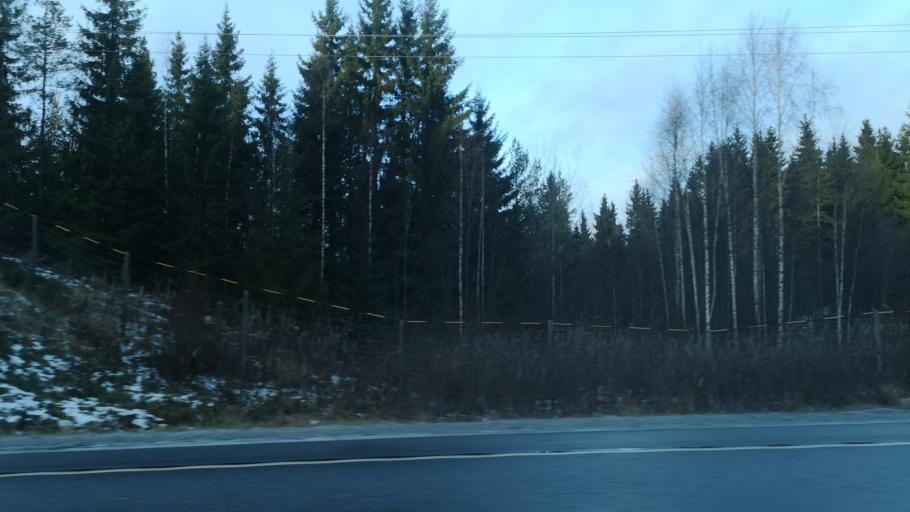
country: FI
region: Southern Savonia
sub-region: Mikkeli
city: Pertunmaa
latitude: 61.4304
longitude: 26.4676
